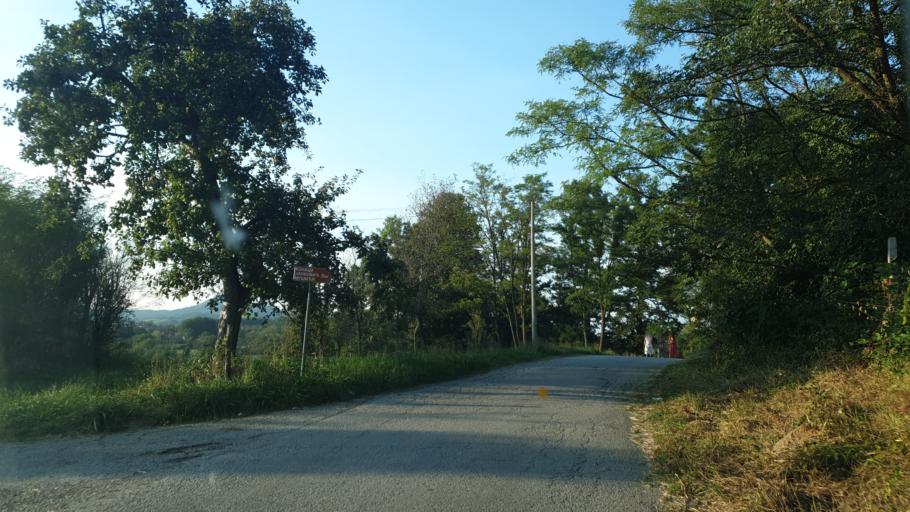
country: RS
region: Central Serbia
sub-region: Zlatiborski Okrug
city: Kosjeric
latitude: 43.9692
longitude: 20.0233
